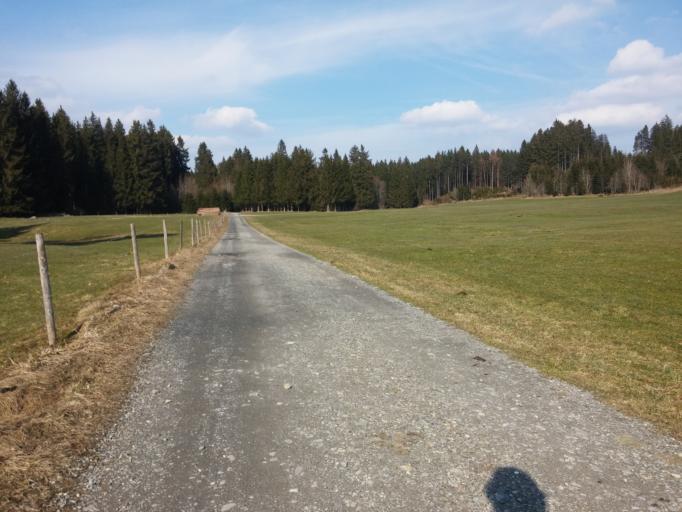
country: DE
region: Bavaria
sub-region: Swabia
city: Betzigau
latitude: 47.7015
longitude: 10.4008
